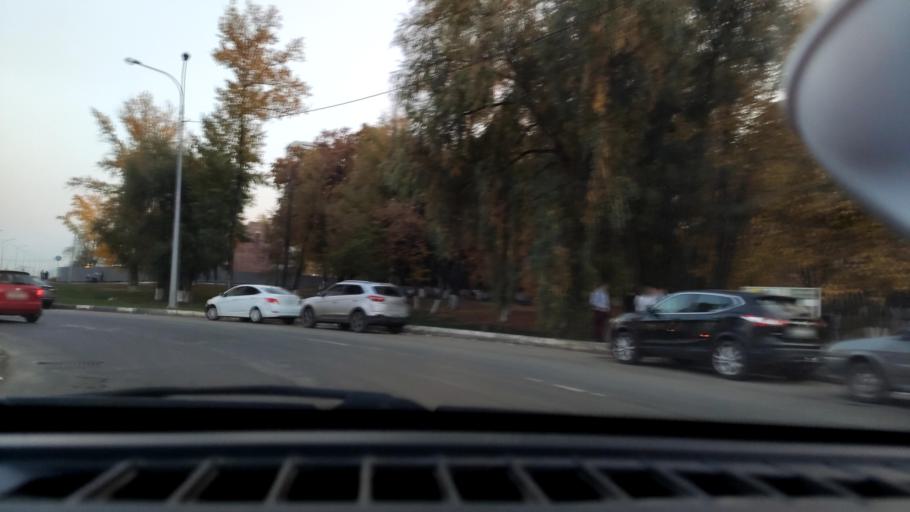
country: RU
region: Samara
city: Rozhdestveno
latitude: 53.1486
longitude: 50.0739
